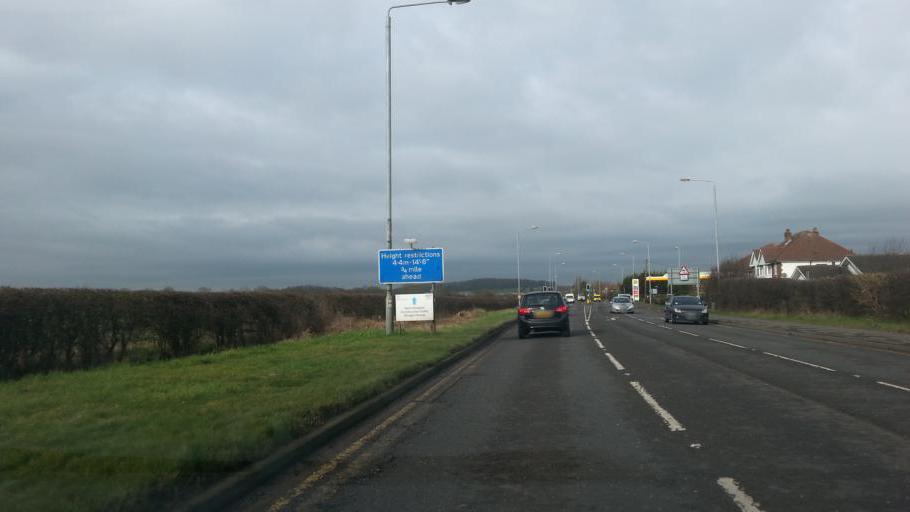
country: GB
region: England
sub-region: Nottinghamshire
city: West Bridgford
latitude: 52.8968
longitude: -1.0947
